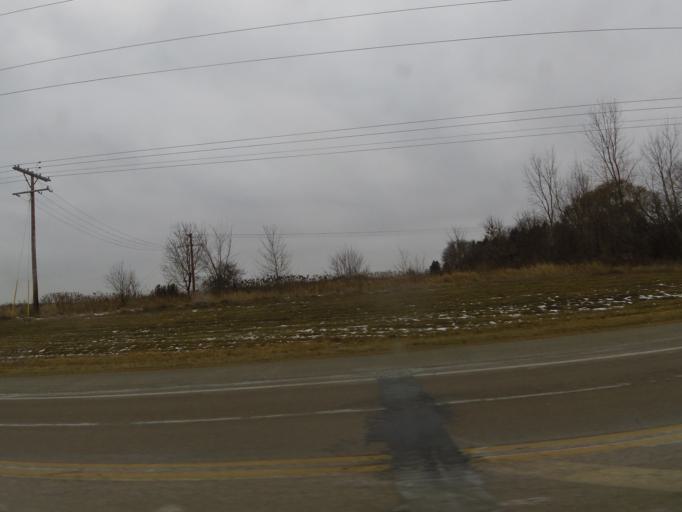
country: US
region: Minnesota
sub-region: Carver County
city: Chaska
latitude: 44.8062
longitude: -93.6411
